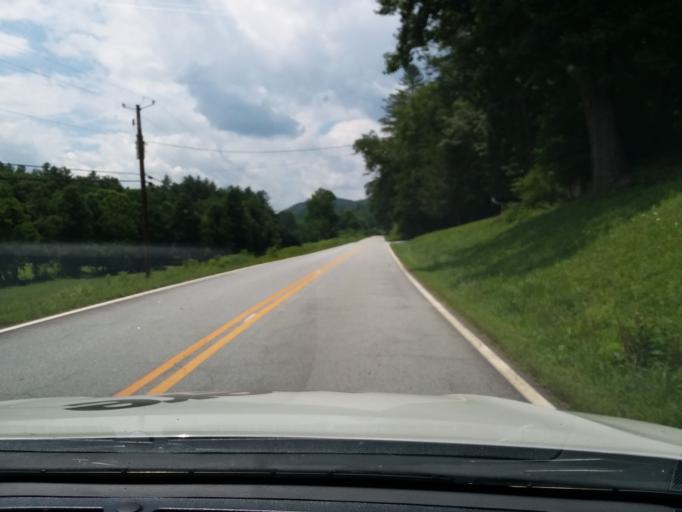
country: US
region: Georgia
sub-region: Rabun County
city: Mountain City
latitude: 34.8869
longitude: -83.3274
